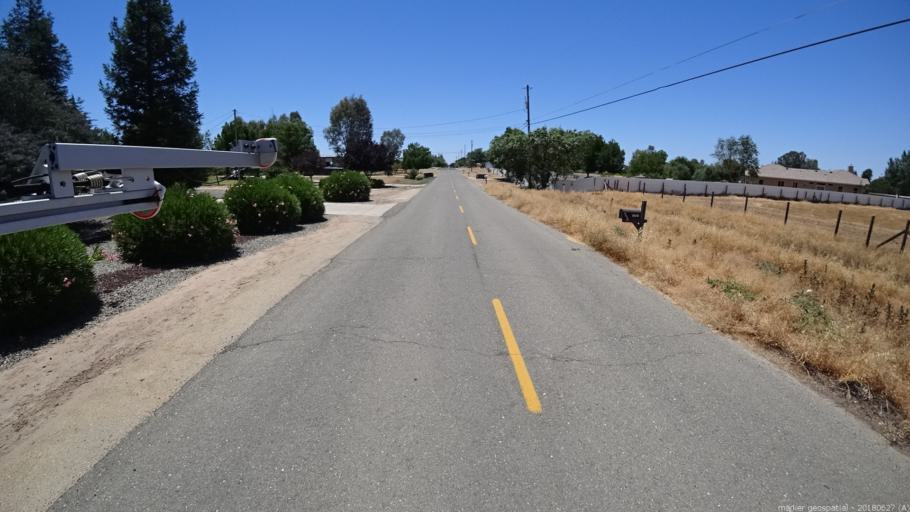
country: US
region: California
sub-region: Madera County
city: Bonadelle Ranchos-Madera Ranchos
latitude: 36.9249
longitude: -119.8655
